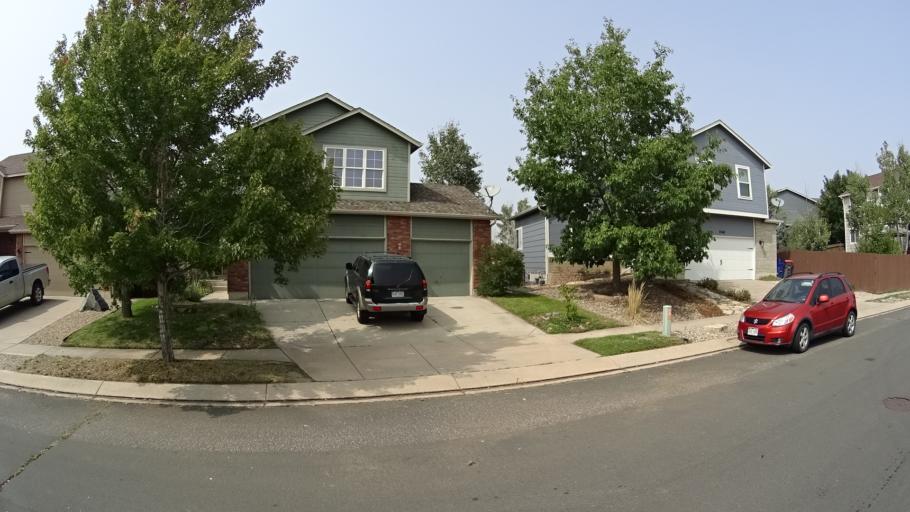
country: US
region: Colorado
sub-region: El Paso County
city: Cimarron Hills
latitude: 38.9261
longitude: -104.7262
